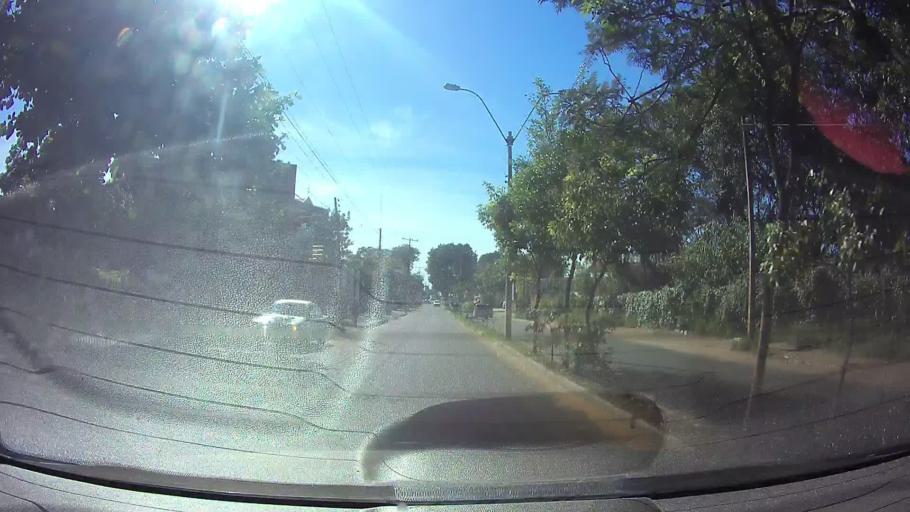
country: PY
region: Central
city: Villa Elisa
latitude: -25.3585
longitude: -57.5727
